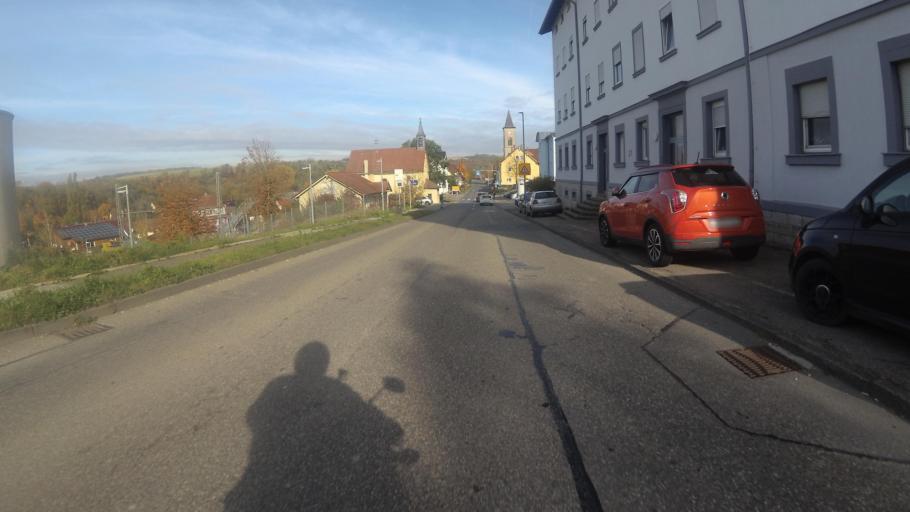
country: DE
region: Baden-Wuerttemberg
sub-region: Regierungsbezirk Stuttgart
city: Mockmuhl
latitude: 49.2938
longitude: 9.3311
